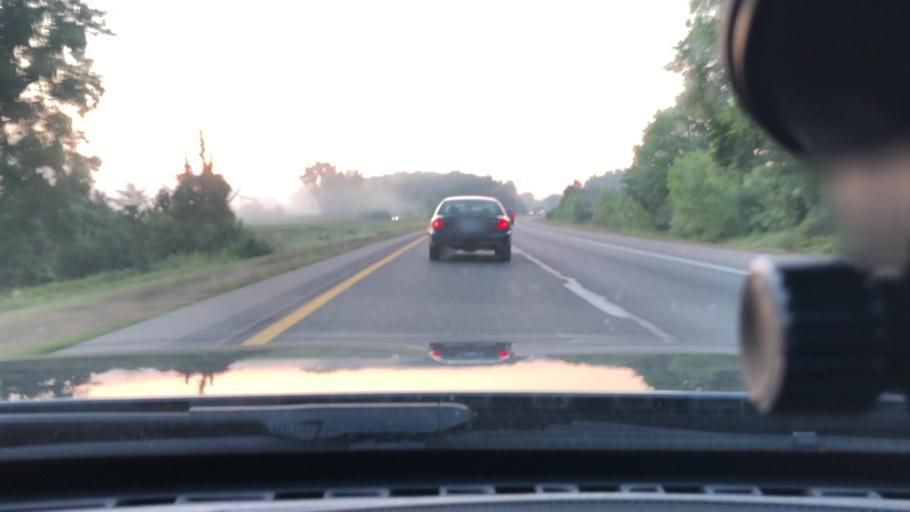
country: US
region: Michigan
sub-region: Washtenaw County
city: Dexter
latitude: 42.2991
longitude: -83.9489
